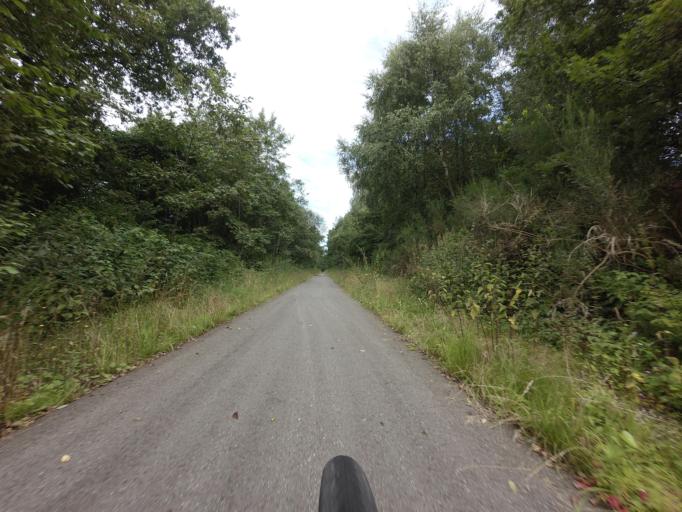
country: DK
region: Central Jutland
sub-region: Norddjurs Kommune
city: Auning
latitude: 56.3980
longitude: 10.4050
